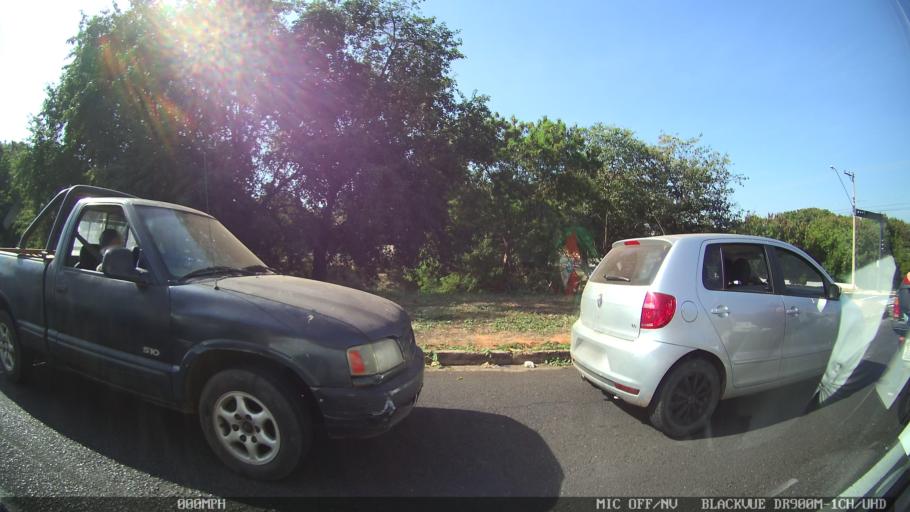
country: BR
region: Sao Paulo
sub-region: Sao Jose Do Rio Preto
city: Sao Jose do Rio Preto
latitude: -20.7955
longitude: -49.4028
